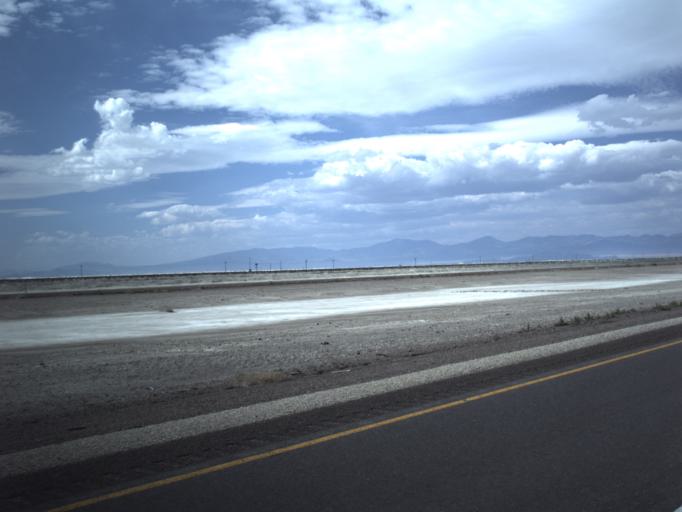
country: US
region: Utah
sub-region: Tooele County
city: Wendover
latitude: 40.7384
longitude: -113.7997
